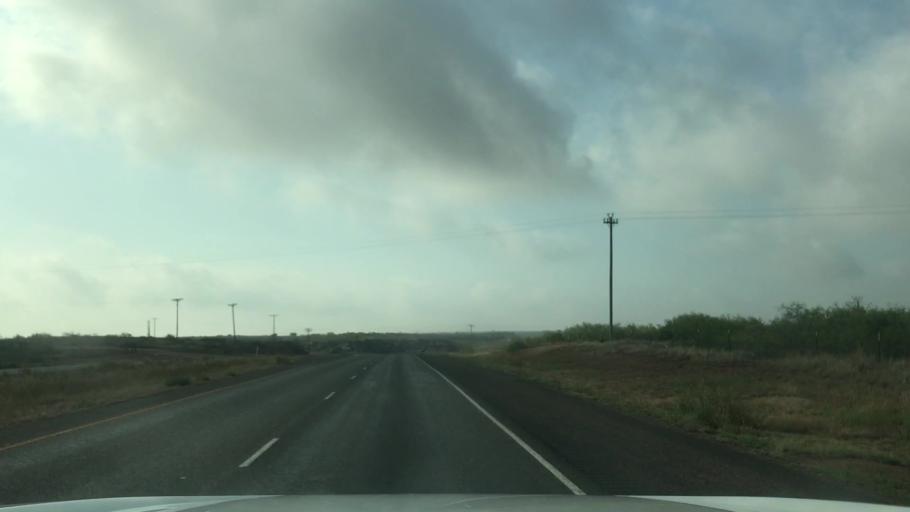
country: US
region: Texas
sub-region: Garza County
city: Post
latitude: 33.1631
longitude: -101.3487
